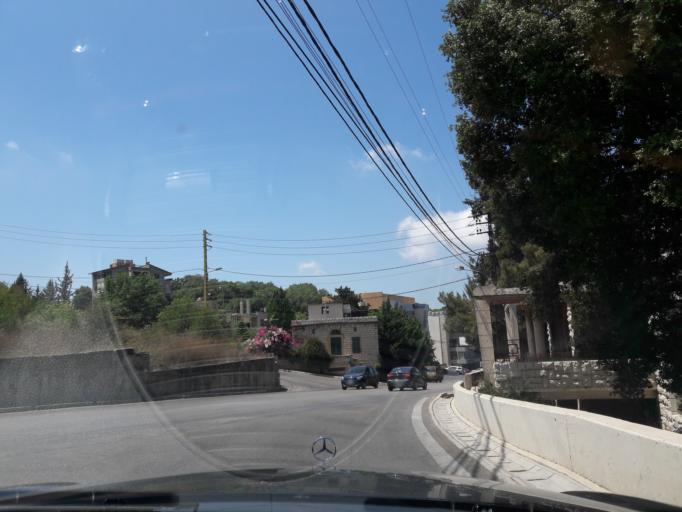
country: LB
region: Mont-Liban
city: Djounie
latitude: 33.9209
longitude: 35.6353
